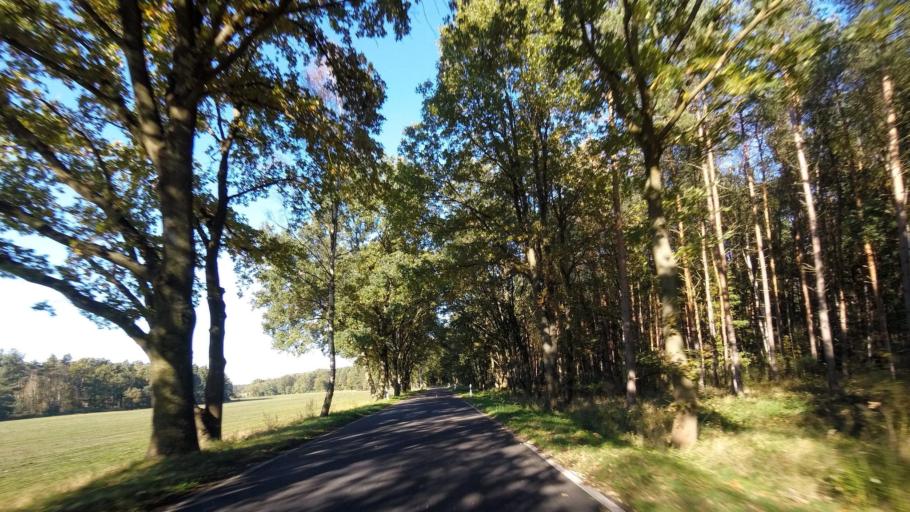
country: DE
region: Saxony-Anhalt
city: Kropstadt
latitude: 51.9648
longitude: 12.7877
